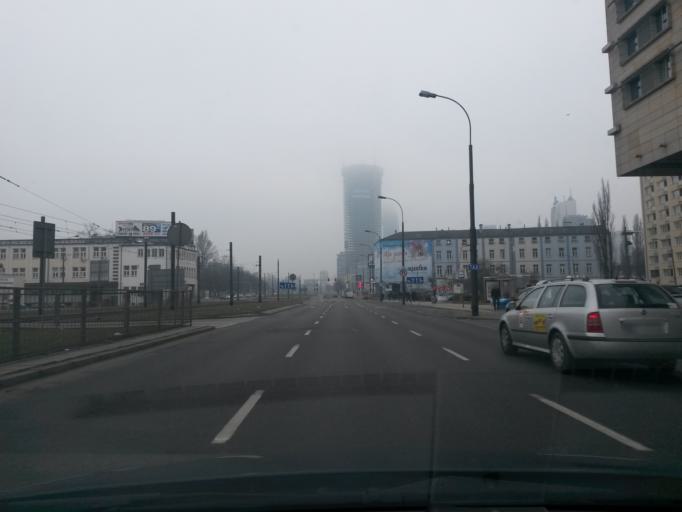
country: PL
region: Masovian Voivodeship
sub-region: Warszawa
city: Ochota
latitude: 52.2259
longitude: 20.9885
